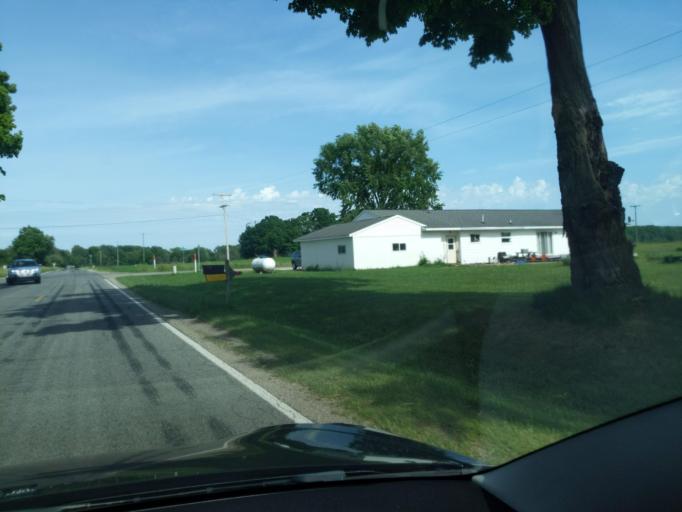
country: US
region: Michigan
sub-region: Newaygo County
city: Fremont
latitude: 43.4238
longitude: -85.9808
